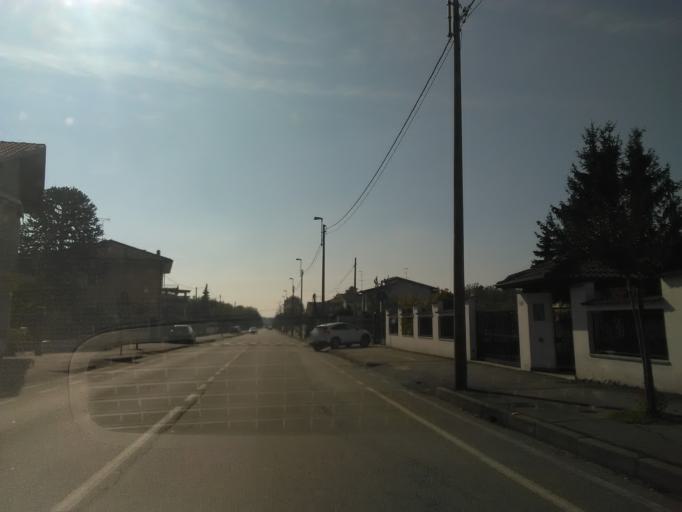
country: IT
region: Piedmont
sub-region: Provincia di Vercelli
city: Gattinara
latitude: 45.6048
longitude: 8.3715
